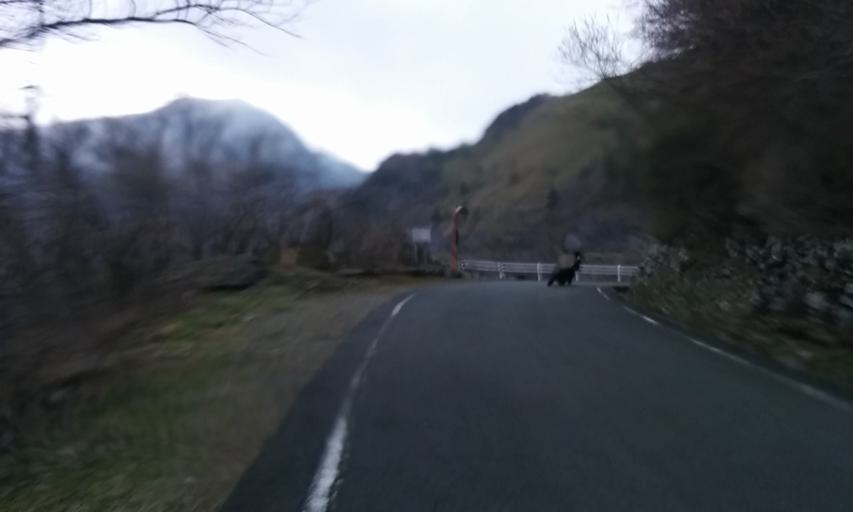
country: JP
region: Ehime
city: Saijo
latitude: 33.7924
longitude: 133.2041
